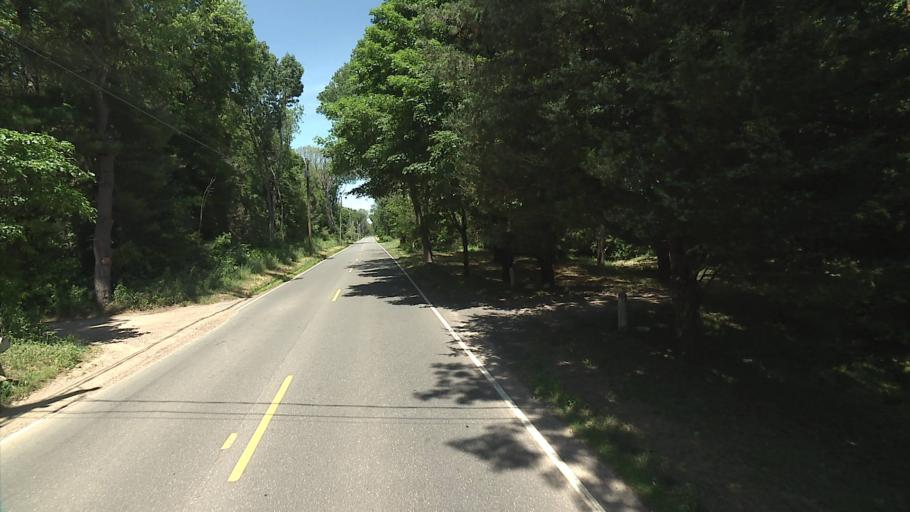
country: US
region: Rhode Island
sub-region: Washington County
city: Ashaway
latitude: 41.4448
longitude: -71.8036
